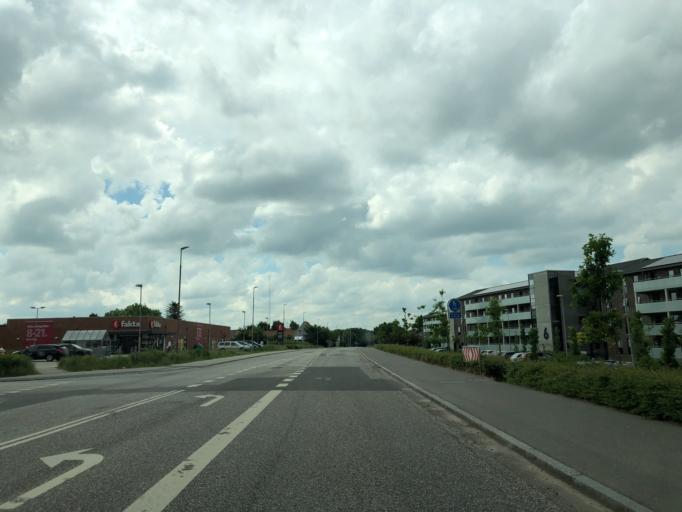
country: DK
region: Central Jutland
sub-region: Struer Kommune
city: Struer
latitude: 56.4844
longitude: 8.5925
